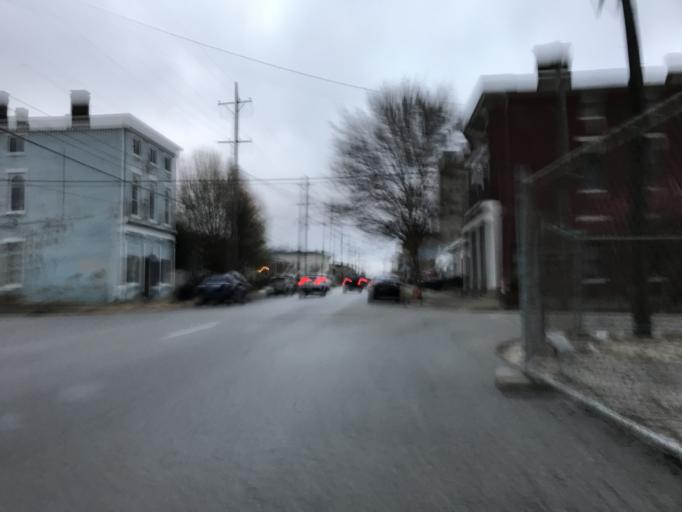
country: US
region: Kentucky
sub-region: Jefferson County
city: Louisville
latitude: 38.2410
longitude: -85.7388
